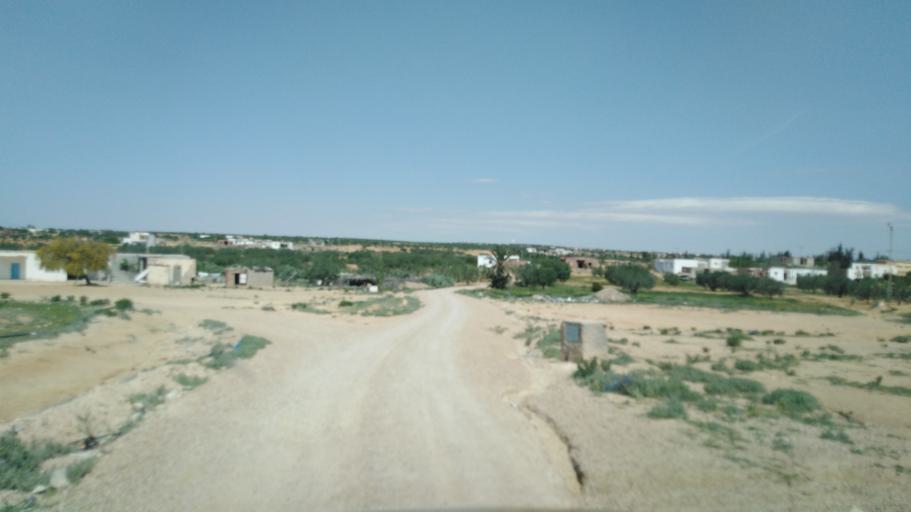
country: TN
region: Safaqis
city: Sfax
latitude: 34.7605
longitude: 10.5250
